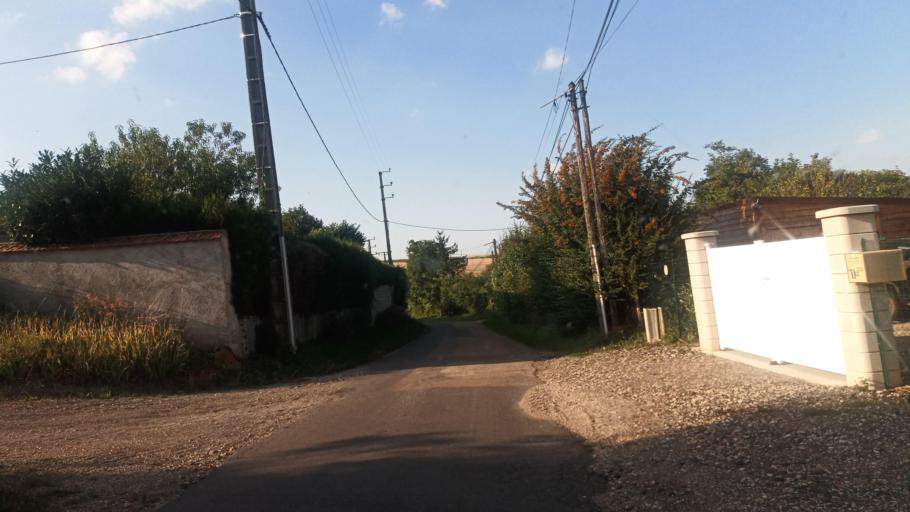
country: FR
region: Bourgogne
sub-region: Departement de l'Yonne
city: Pont-sur-Yonne
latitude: 48.2593
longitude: 3.1792
